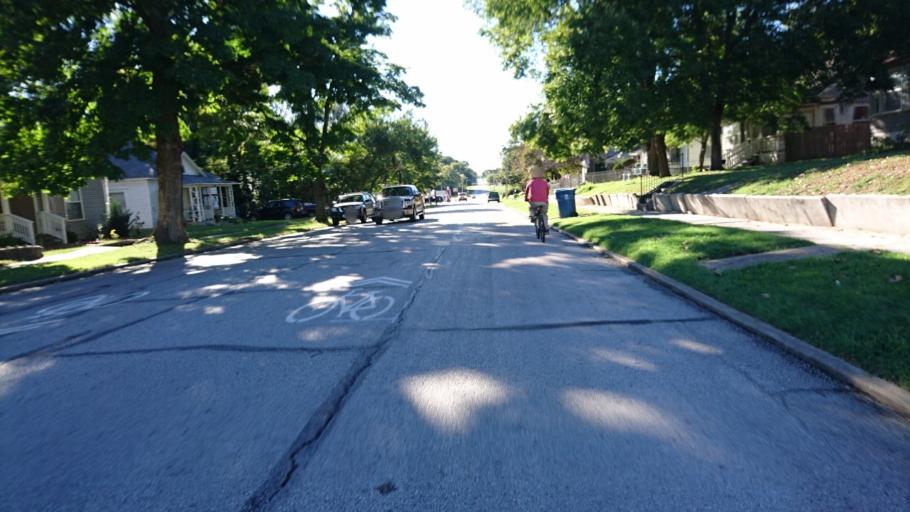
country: US
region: Missouri
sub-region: Jasper County
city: Carthage
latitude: 37.1766
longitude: -94.3247
